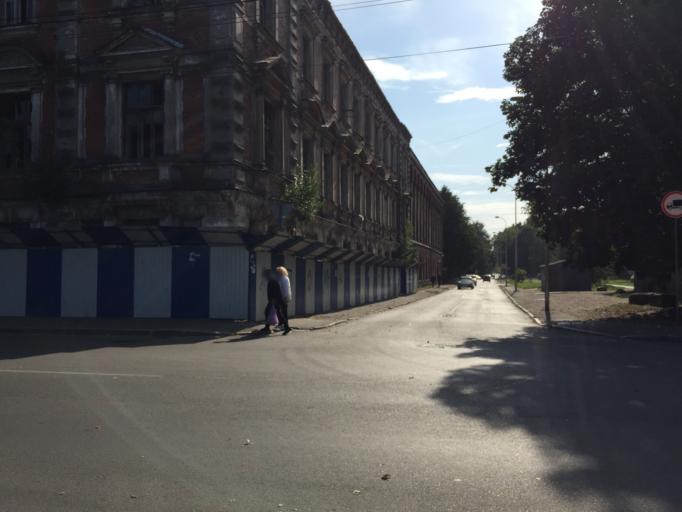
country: RU
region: Kaliningrad
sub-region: Gorod Kaliningrad
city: Kaliningrad
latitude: 54.7045
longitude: 20.5034
